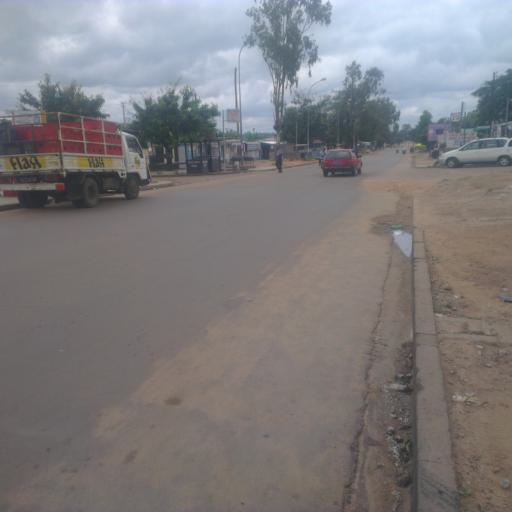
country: CI
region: Vallee du Bandama
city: Bouake
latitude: 7.6793
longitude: -5.0257
